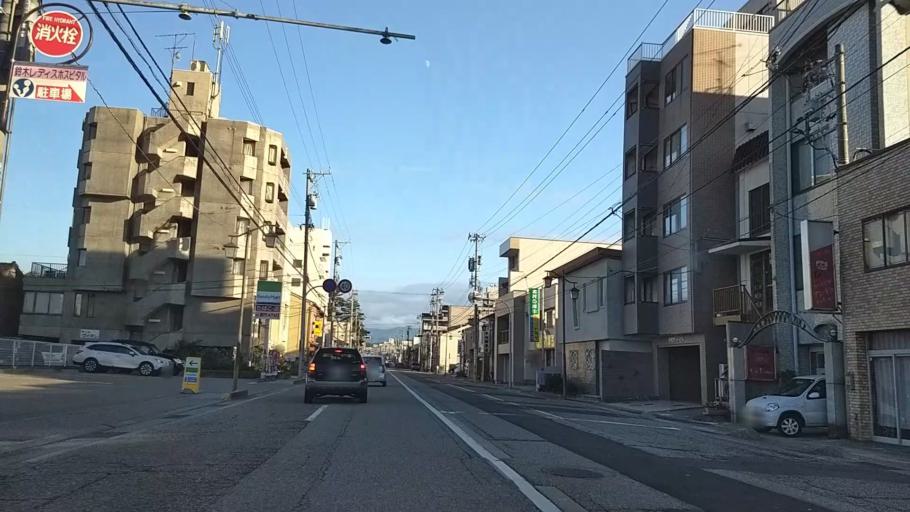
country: JP
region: Ishikawa
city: Nonoichi
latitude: 36.5490
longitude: 136.6568
